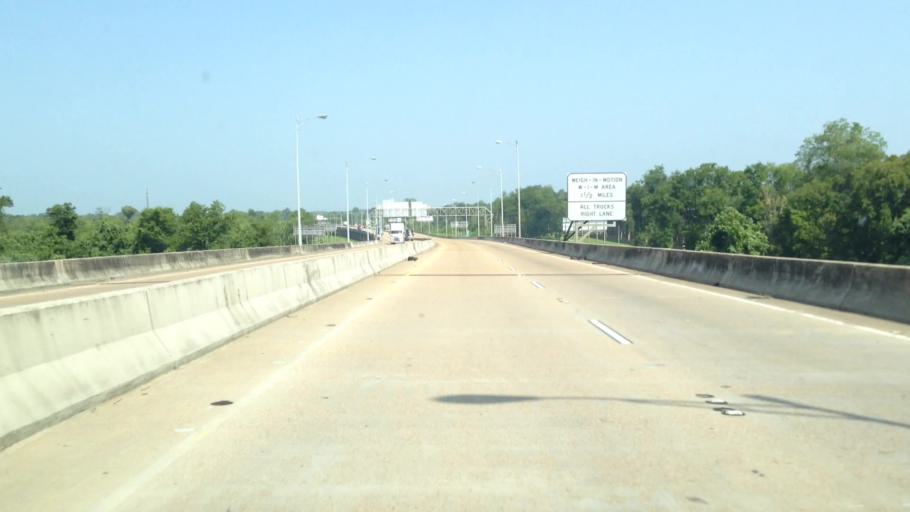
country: US
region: Mississippi
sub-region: Warren County
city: Vicksburg
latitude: 32.3166
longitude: -90.9112
